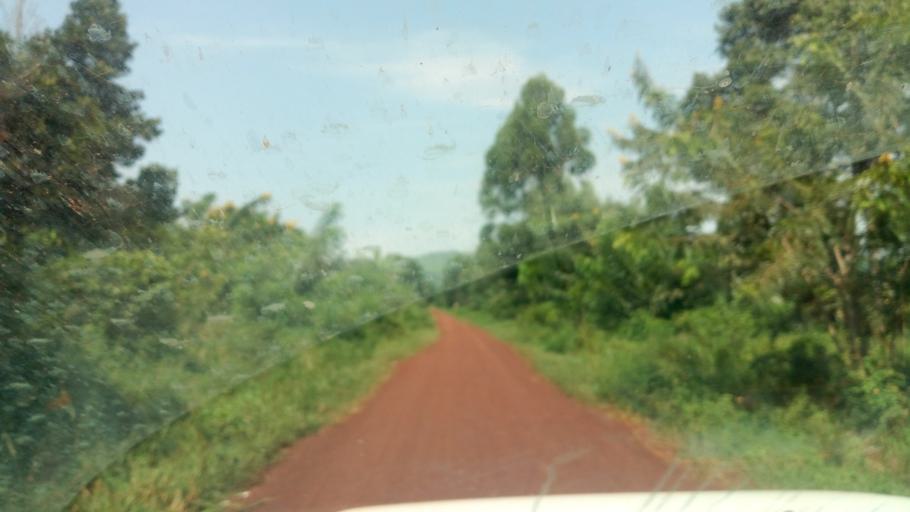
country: UG
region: Western Region
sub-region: Masindi District
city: Masindi
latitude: 1.6626
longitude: 31.8132
